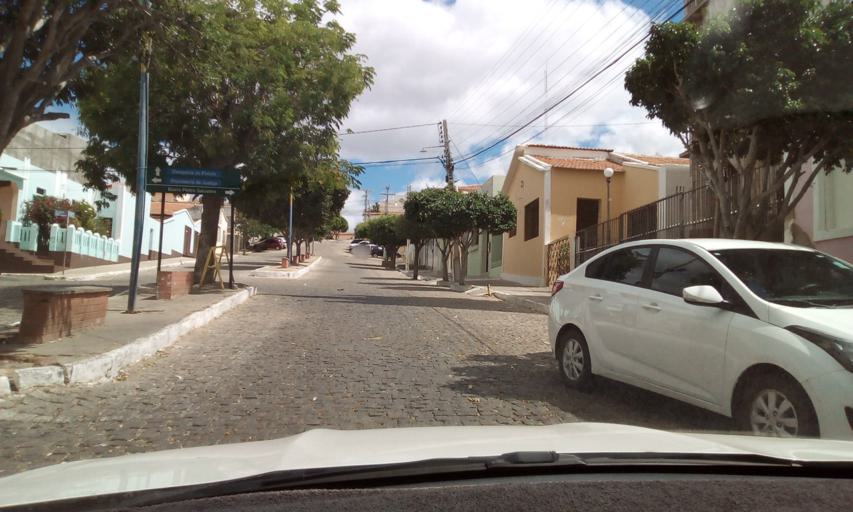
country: BR
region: Paraiba
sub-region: Picui
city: Picui
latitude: -6.5087
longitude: -36.3468
